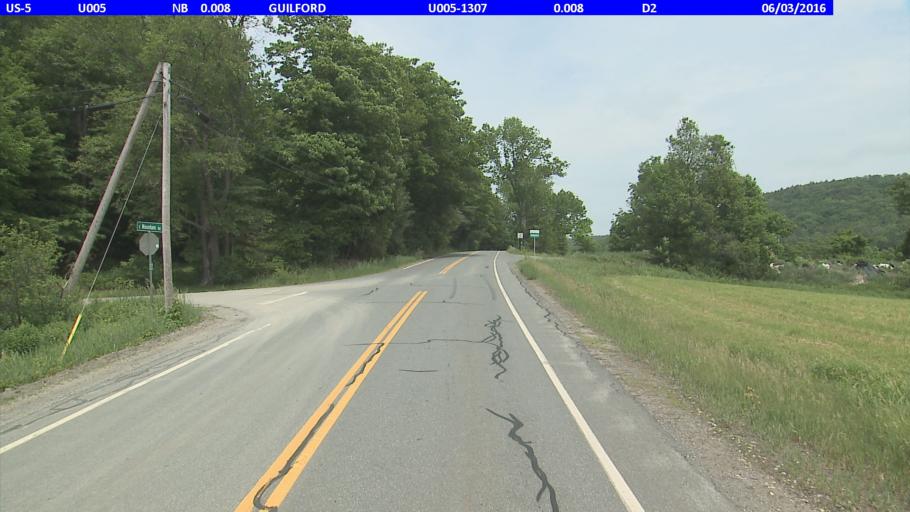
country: US
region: Massachusetts
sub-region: Franklin County
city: Bernardston
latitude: 42.7303
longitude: -72.5731
